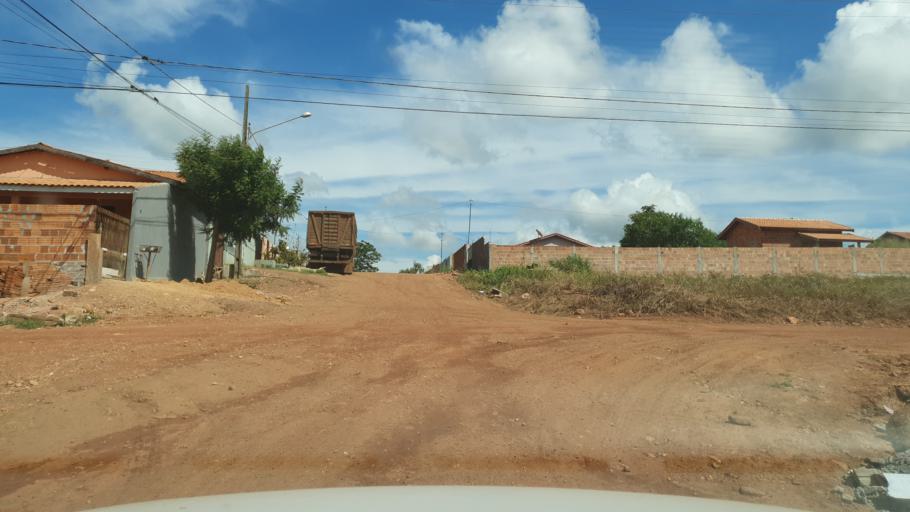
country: BR
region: Mato Grosso
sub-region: Pontes E Lacerda
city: Pontes e Lacerda
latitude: -15.2506
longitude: -59.3140
